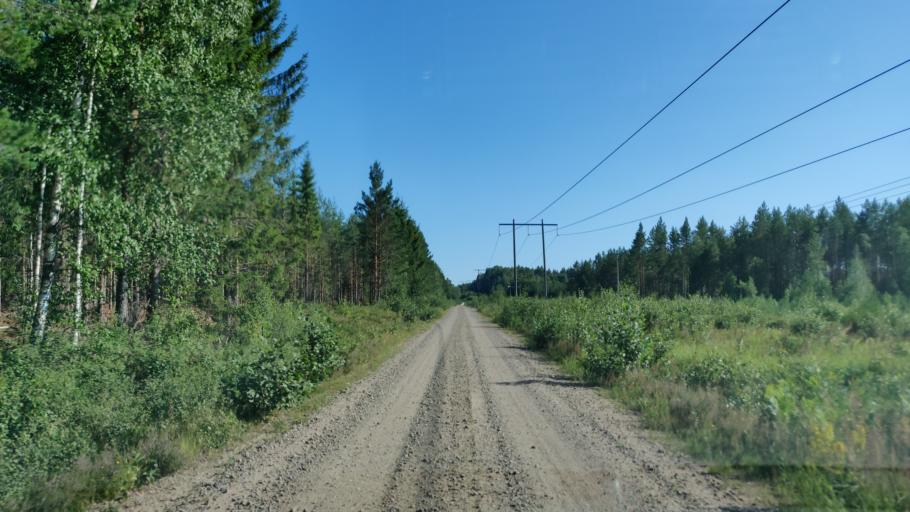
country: SE
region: Vaermland
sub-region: Hagfors Kommun
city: Ekshaerad
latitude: 60.0521
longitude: 13.5224
